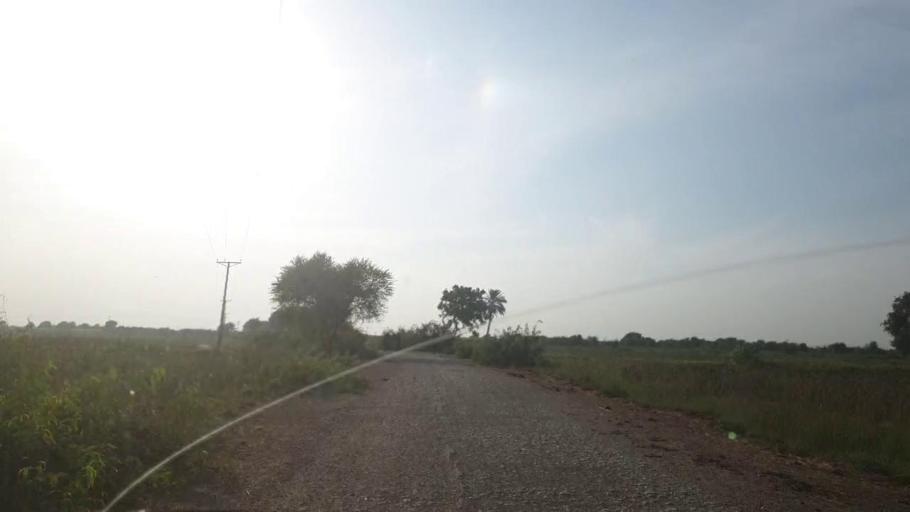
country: PK
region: Sindh
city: Tando Muhammad Khan
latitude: 25.2222
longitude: 68.5352
